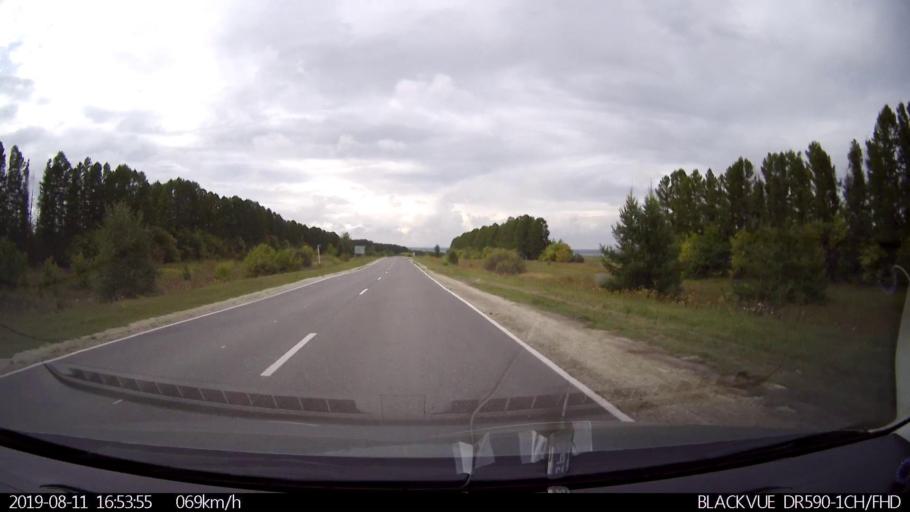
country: RU
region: Ulyanovsk
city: Mayna
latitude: 54.2676
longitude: 47.6682
